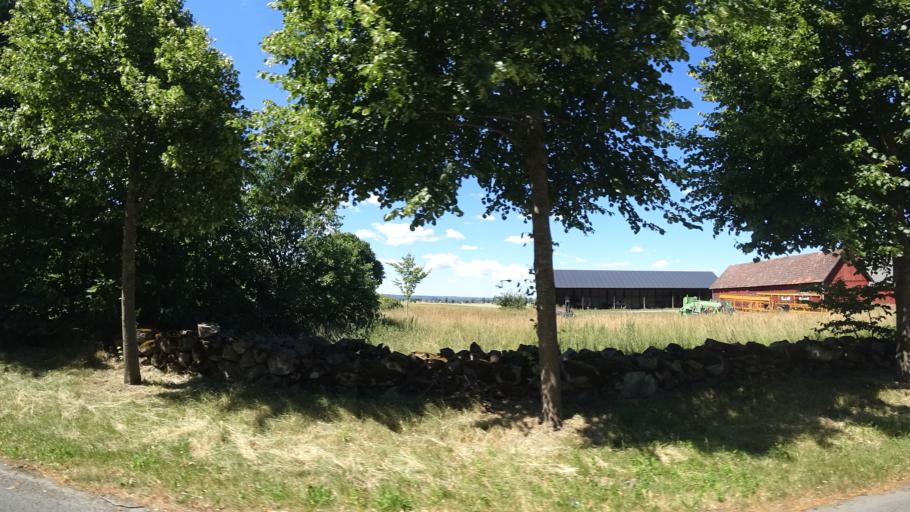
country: SE
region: Skane
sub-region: Kristianstads Kommun
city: Onnestad
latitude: 56.0690
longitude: 14.0839
